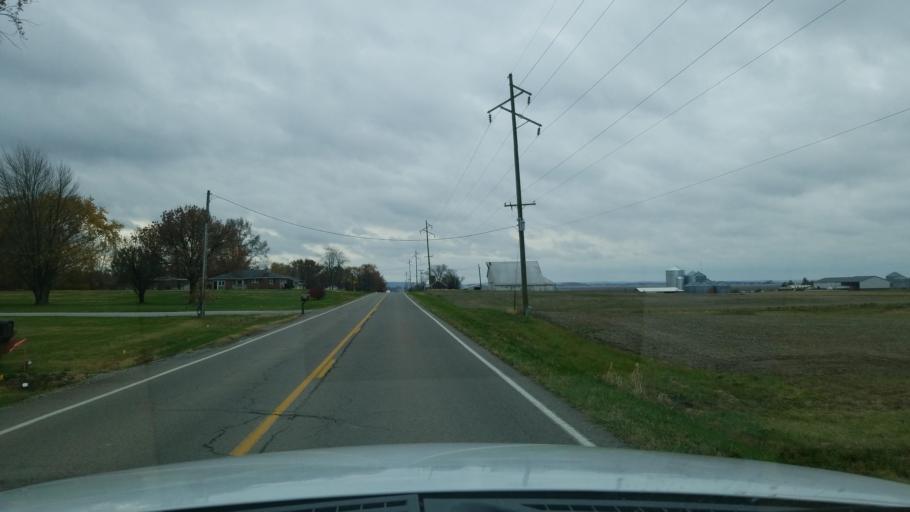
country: US
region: Illinois
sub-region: Saline County
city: Eldorado
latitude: 37.7962
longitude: -88.4383
